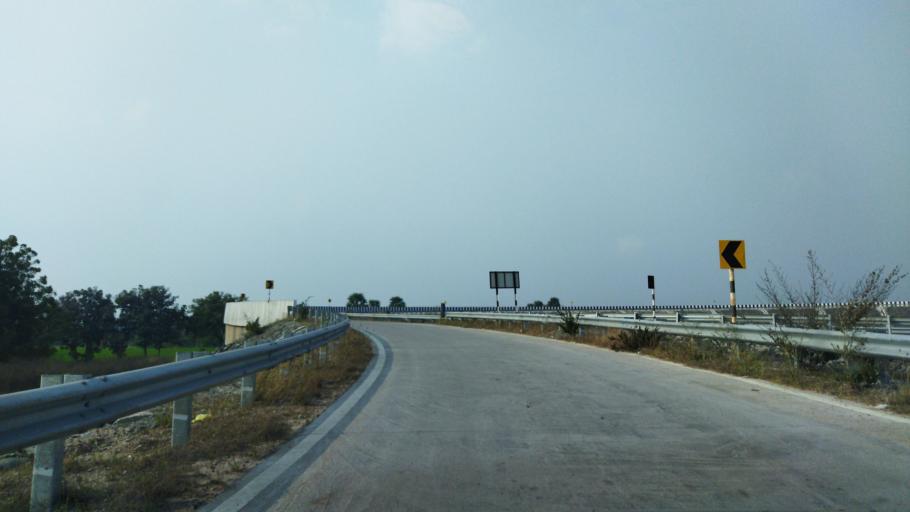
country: IN
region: Telangana
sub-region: Nalgonda
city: Nalgonda
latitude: 17.1681
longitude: 79.3969
